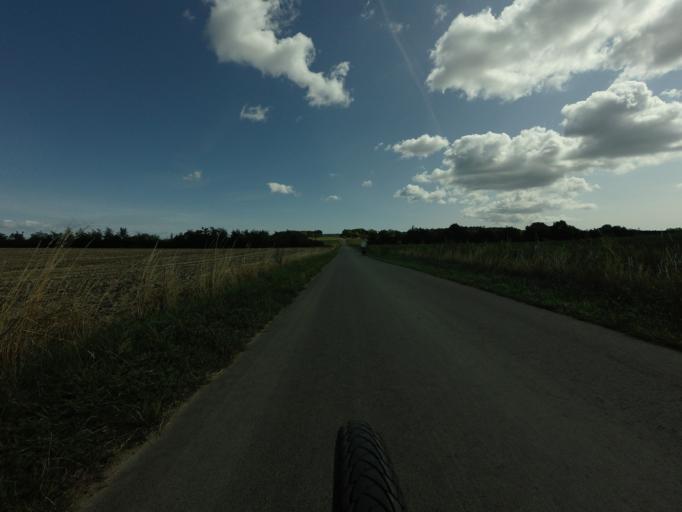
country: DK
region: Zealand
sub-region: Vordingborg Kommune
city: Stege
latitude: 54.9724
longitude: 12.4339
